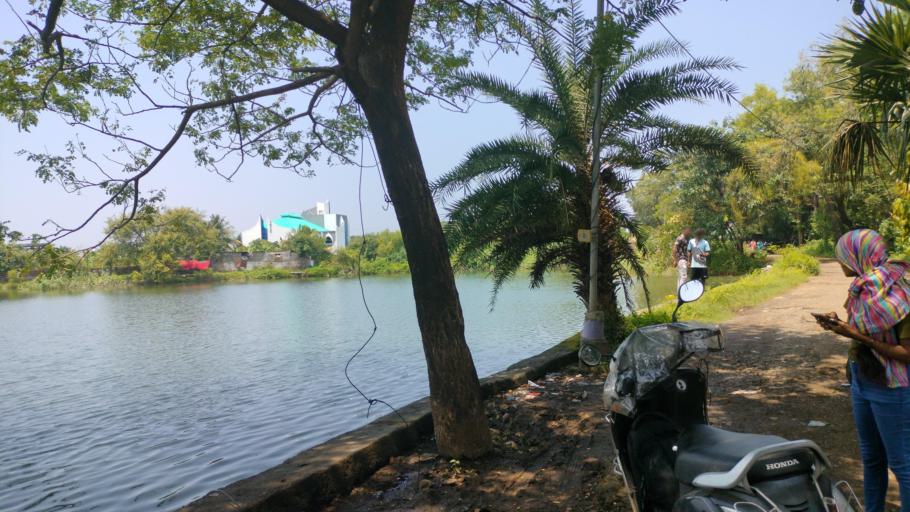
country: IN
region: Maharashtra
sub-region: Thane
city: Virar
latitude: 19.3873
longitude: 72.7831
